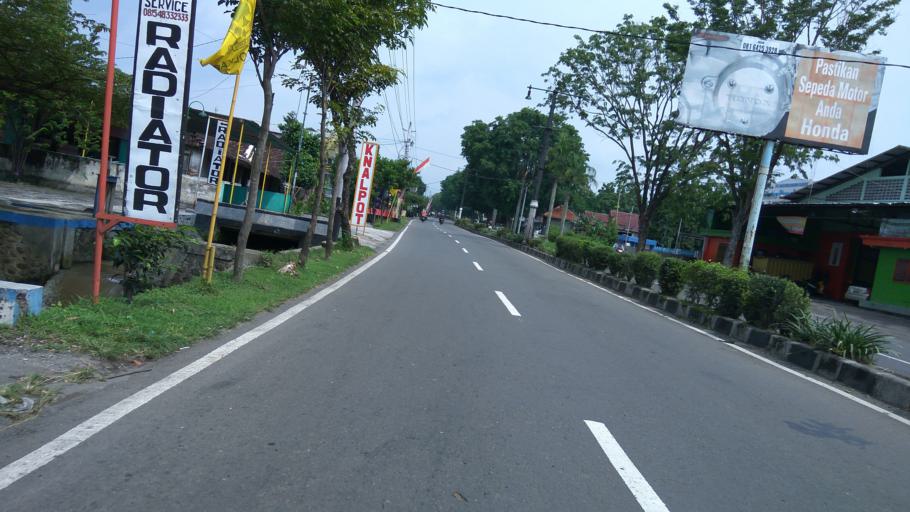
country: ID
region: Central Java
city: Jaten
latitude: -7.5874
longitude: 110.9210
